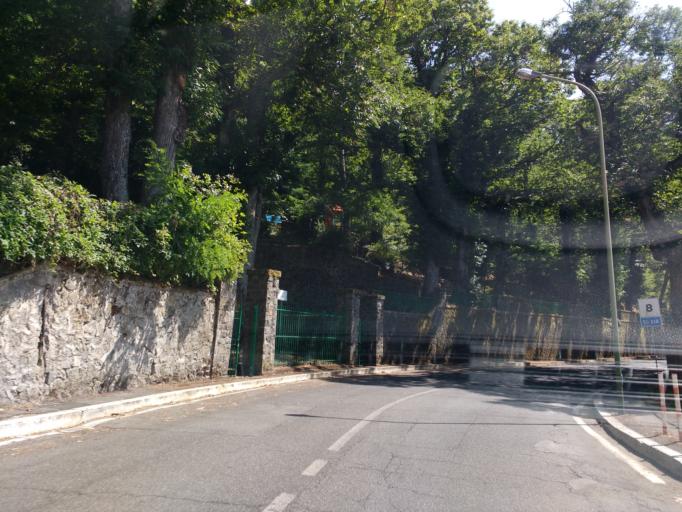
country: IT
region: Latium
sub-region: Citta metropolitana di Roma Capitale
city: Rocca di Papa
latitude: 41.7554
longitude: 12.7062
